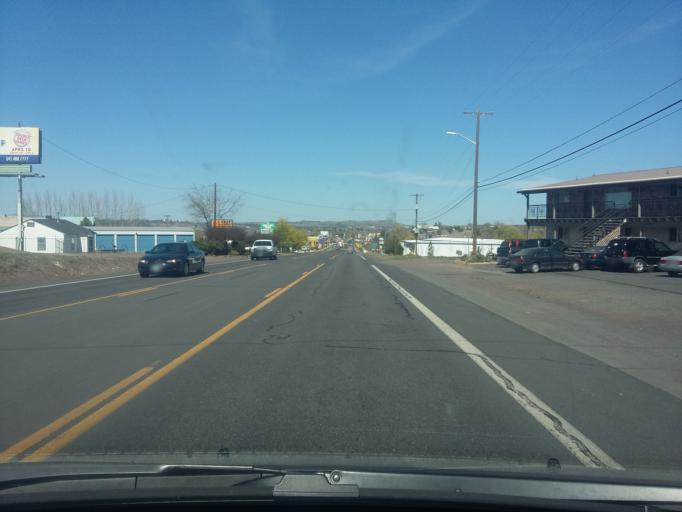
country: US
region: Oregon
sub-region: Jefferson County
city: Madras
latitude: 44.6152
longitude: -121.1349
